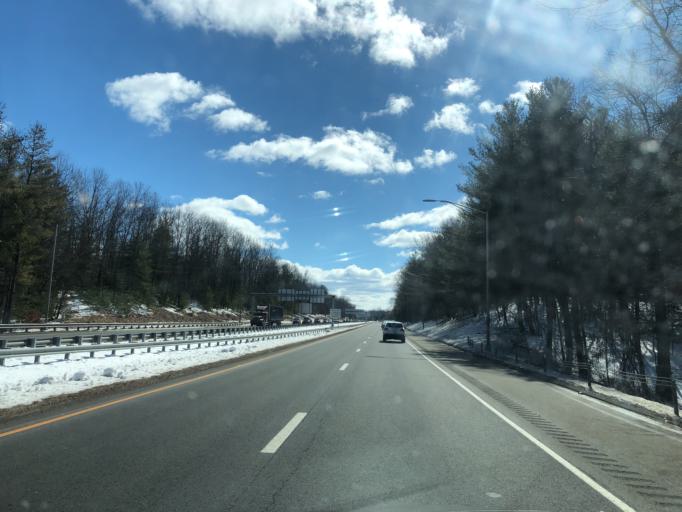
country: US
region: Connecticut
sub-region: Hartford County
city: Windsor Locks
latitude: 41.9139
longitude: -72.6713
